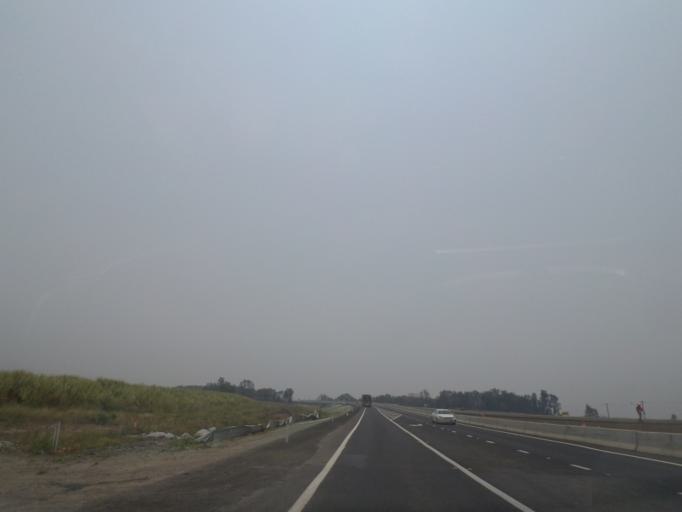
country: AU
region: New South Wales
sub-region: Clarence Valley
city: Maclean
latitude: -29.4076
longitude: 153.2424
